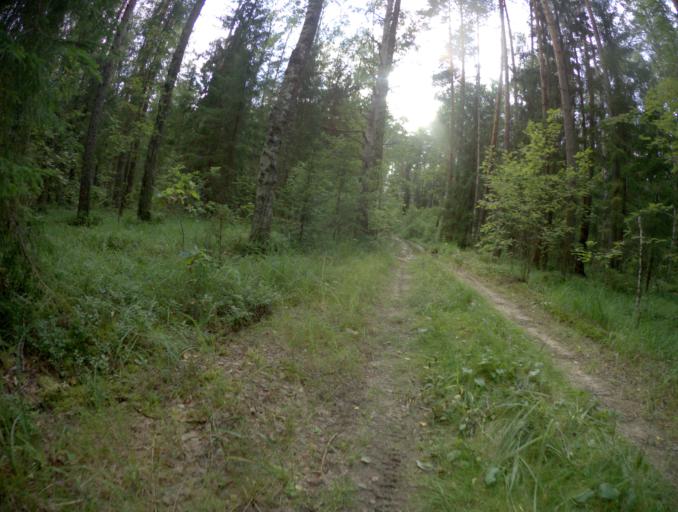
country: RU
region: Vladimir
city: Orgtrud
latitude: 56.1259
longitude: 40.5751
